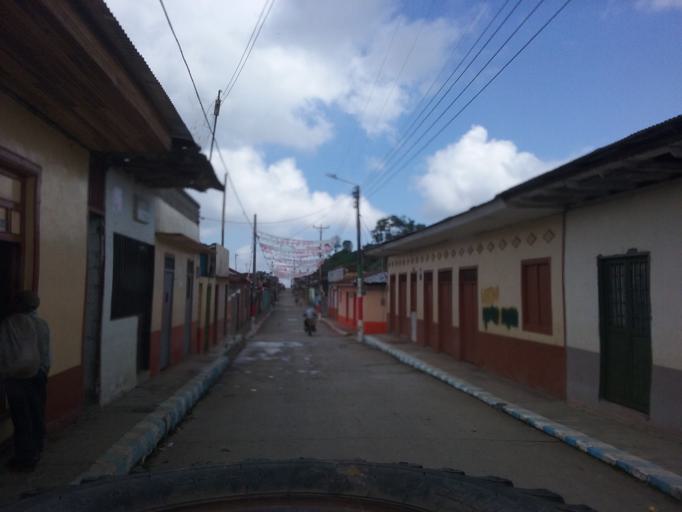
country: CO
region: Tolima
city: Libano
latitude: 4.7984
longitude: -75.0509
